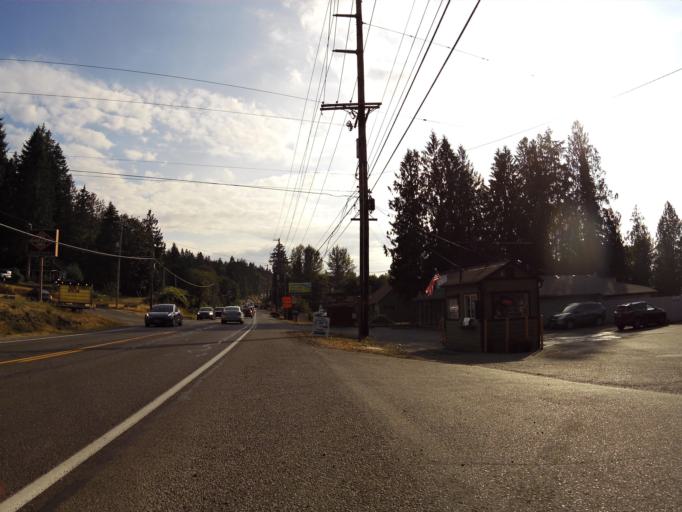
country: US
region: Washington
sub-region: Mason County
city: Belfair
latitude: 47.4356
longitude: -122.8388
